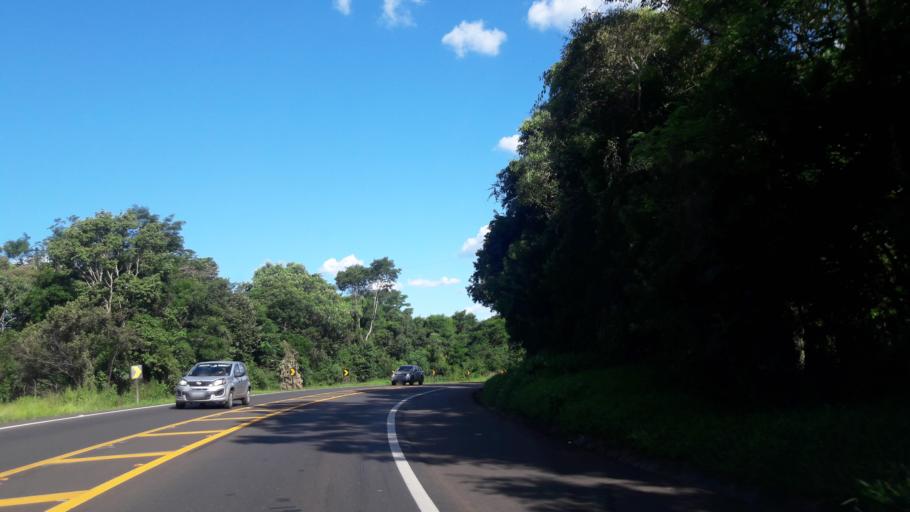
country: BR
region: Parana
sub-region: Laranjeiras Do Sul
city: Laranjeiras do Sul
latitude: -25.4192
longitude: -52.0337
